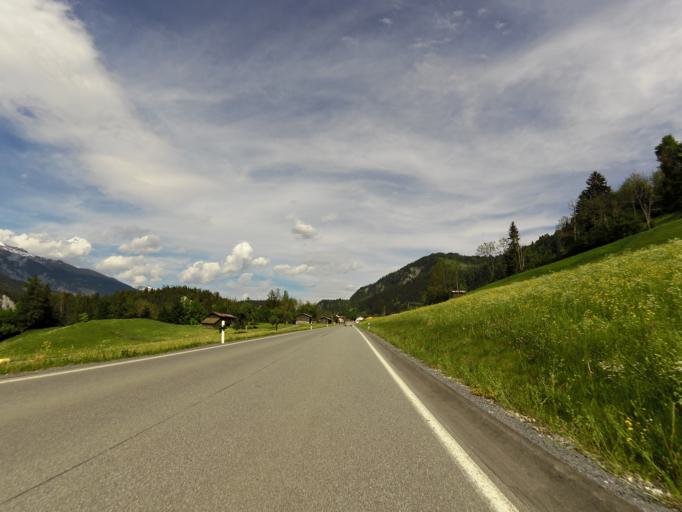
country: CH
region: Grisons
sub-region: Surselva District
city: Laax
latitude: 46.7867
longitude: 9.2725
